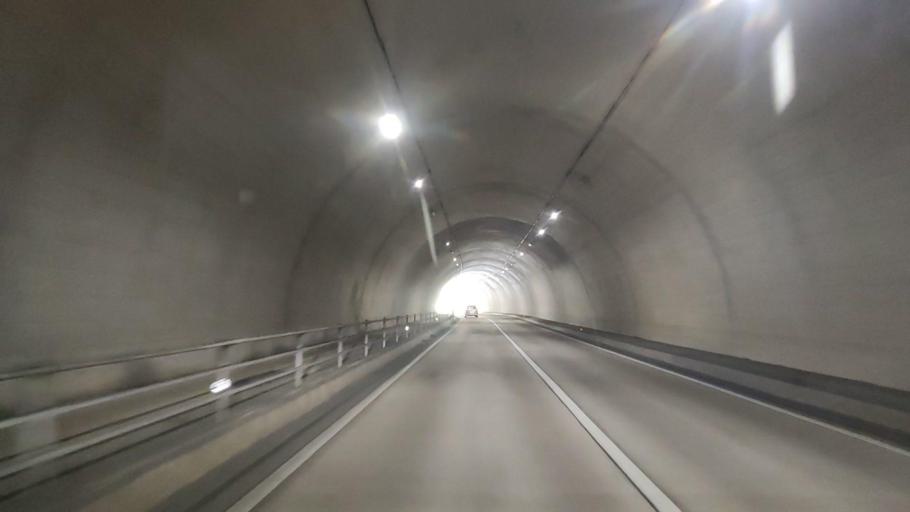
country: JP
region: Gifu
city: Godo
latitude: 35.5594
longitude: 136.6407
